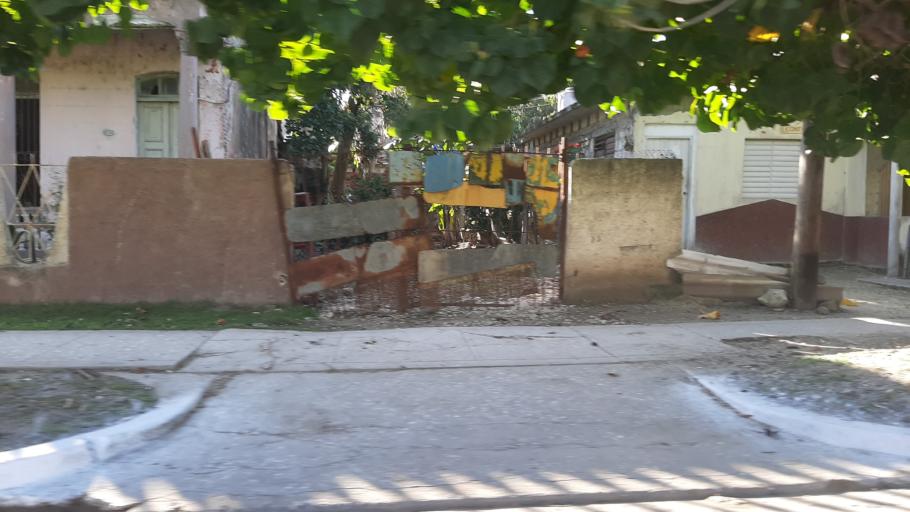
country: CU
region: Villa Clara
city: Santa Clara
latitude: 22.4126
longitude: -79.9548
